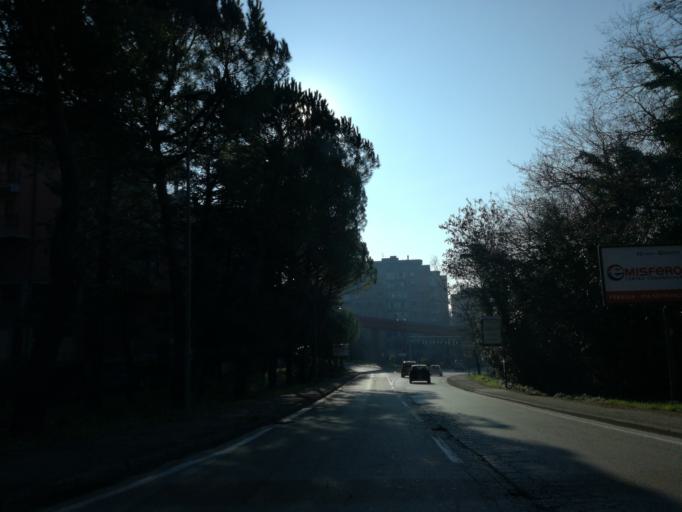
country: IT
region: Umbria
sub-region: Provincia di Perugia
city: Perugia
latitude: 43.1099
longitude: 12.3771
